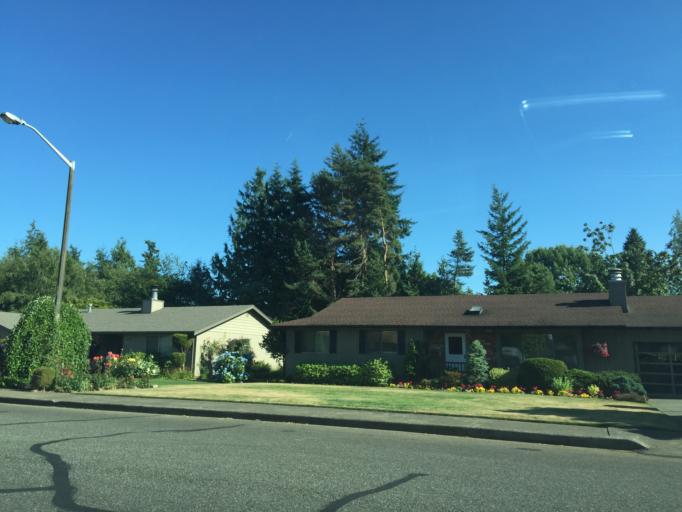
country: US
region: Washington
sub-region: Whatcom County
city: Lynden
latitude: 48.9538
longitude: -122.4385
